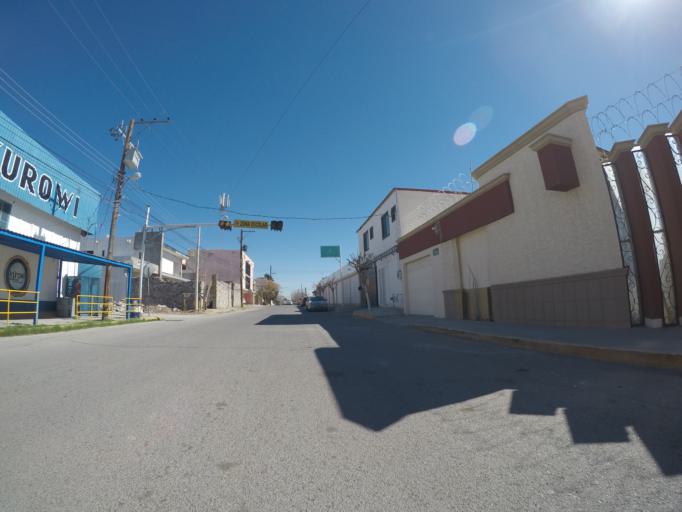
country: MX
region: Chihuahua
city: Ciudad Juarez
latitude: 31.7325
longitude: -106.4465
